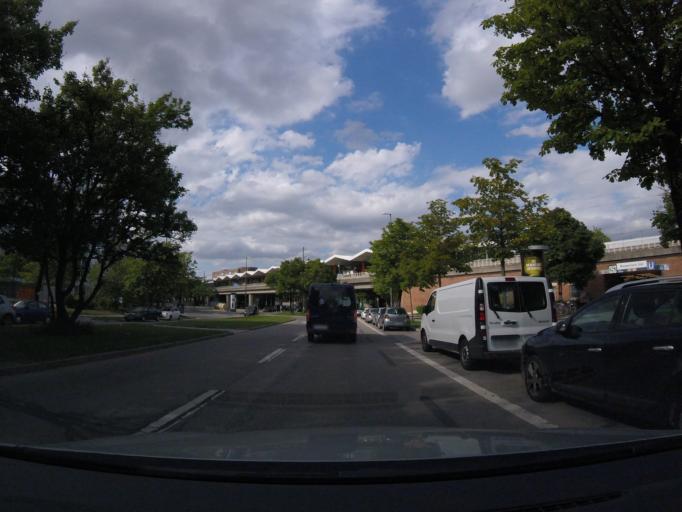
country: DE
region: Bavaria
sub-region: Upper Bavaria
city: Neubiberg
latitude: 48.0878
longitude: 11.6452
